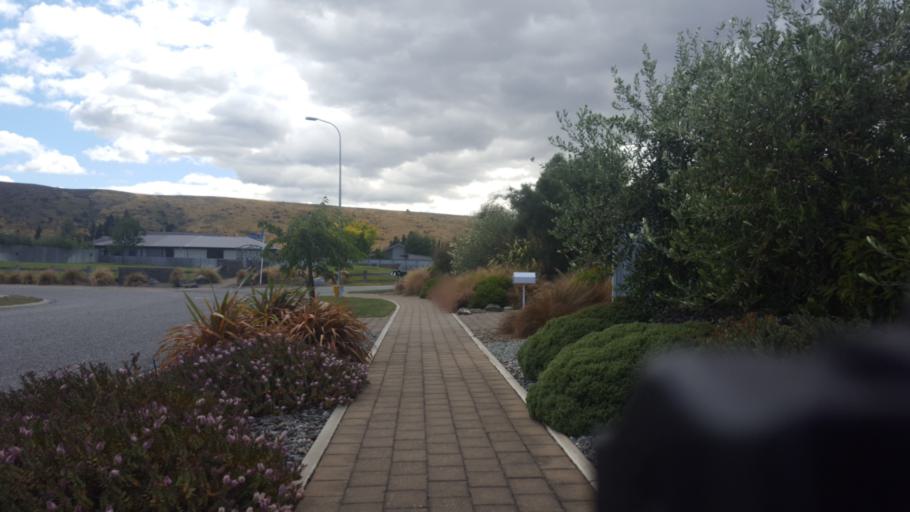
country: NZ
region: Otago
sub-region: Queenstown-Lakes District
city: Wanaka
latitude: -45.1963
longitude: 169.3326
